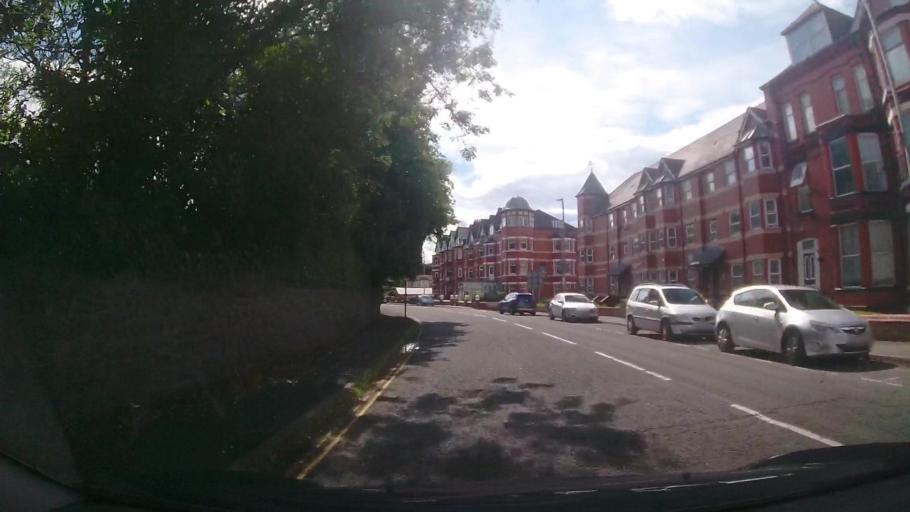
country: GB
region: Wales
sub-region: Sir Powys
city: Llandrindod Wells
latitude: 52.2378
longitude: -3.3782
